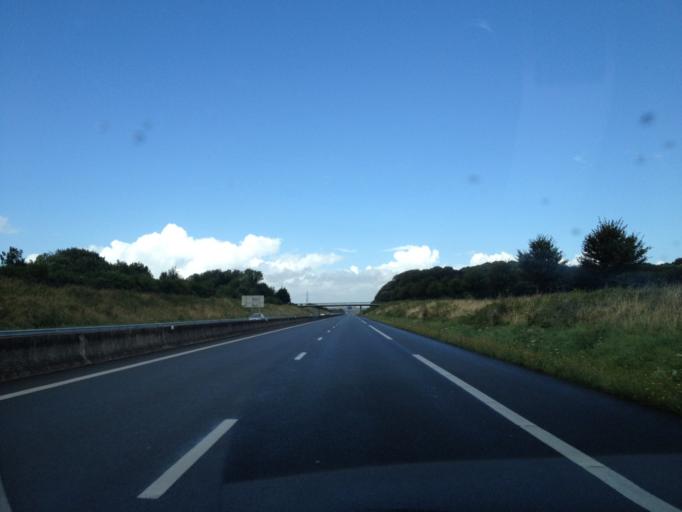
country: FR
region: Nord-Pas-de-Calais
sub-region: Departement du Pas-de-Calais
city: Verton
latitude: 50.3984
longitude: 1.6943
